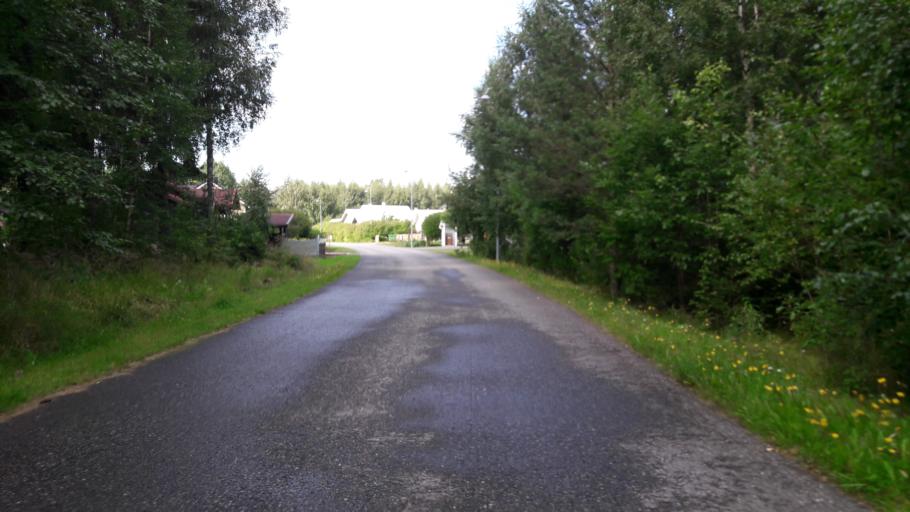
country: FI
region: North Karelia
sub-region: Joensuu
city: Joensuu
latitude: 62.5108
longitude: 29.8272
